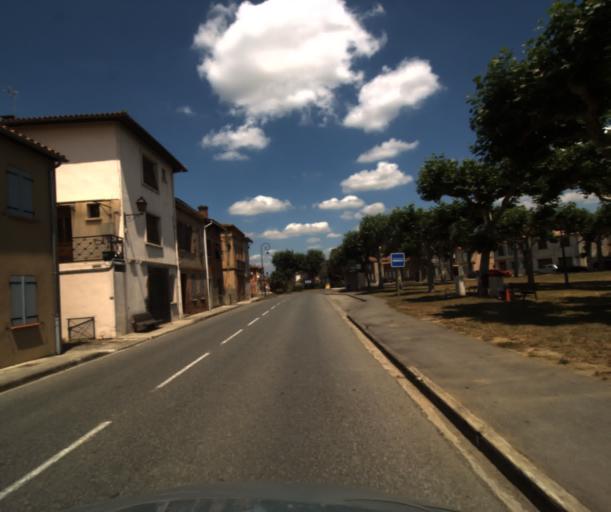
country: FR
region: Midi-Pyrenees
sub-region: Departement de la Haute-Garonne
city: Labastidette
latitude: 43.4656
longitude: 1.2160
